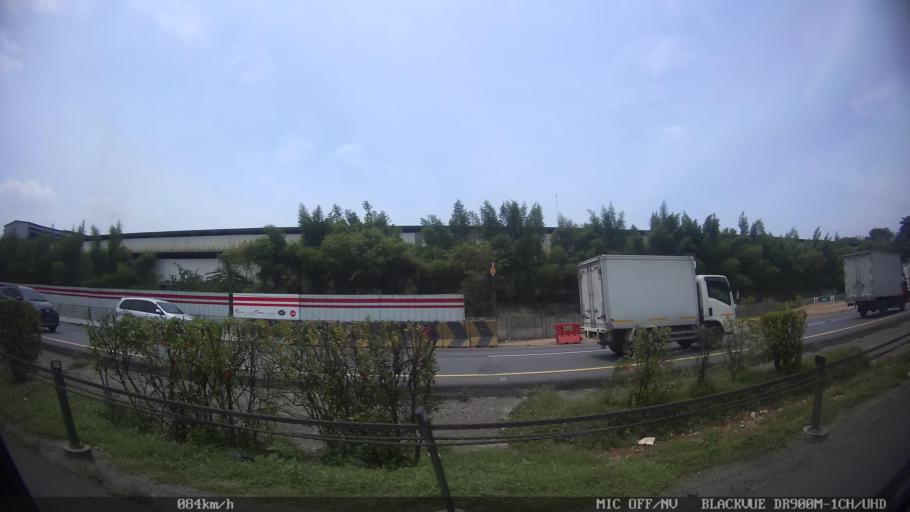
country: ID
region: West Java
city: Kresek
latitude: -6.1673
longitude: 106.3378
